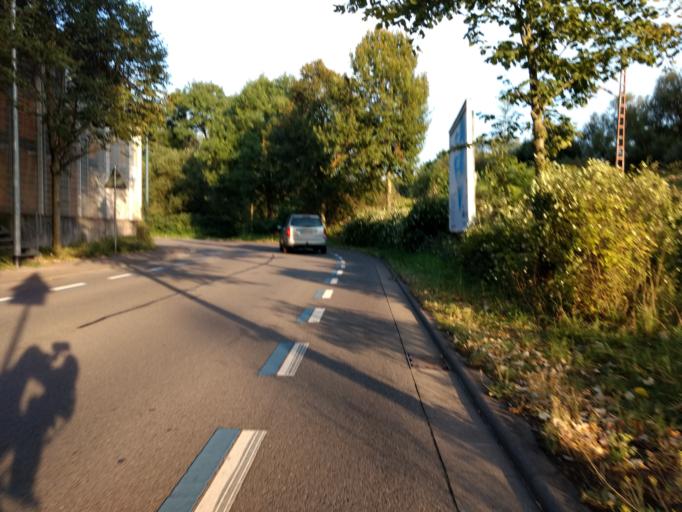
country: DE
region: Saarland
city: Dillingen
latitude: 49.3473
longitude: 6.7297
